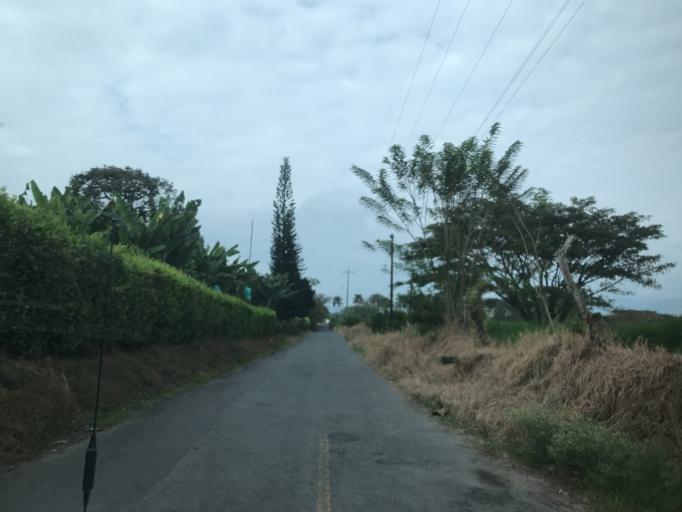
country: CO
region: Quindio
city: Montenegro
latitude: 4.5549
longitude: -75.7878
